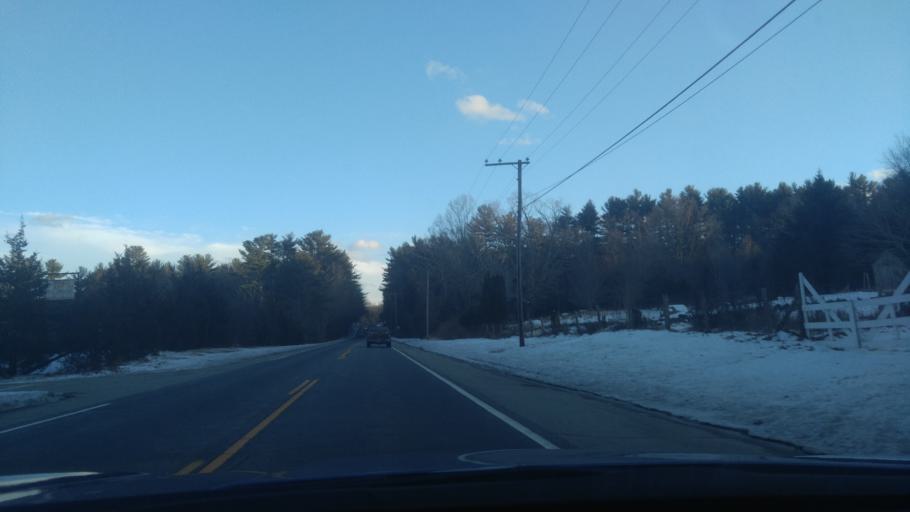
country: US
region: Rhode Island
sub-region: Kent County
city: Coventry
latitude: 41.7073
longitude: -71.6440
